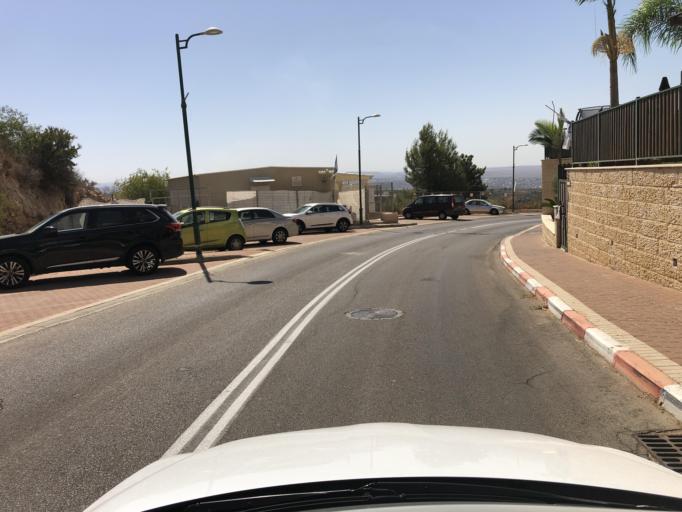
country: PS
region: West Bank
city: An Nabi Ilyas
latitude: 32.1672
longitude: 35.0217
